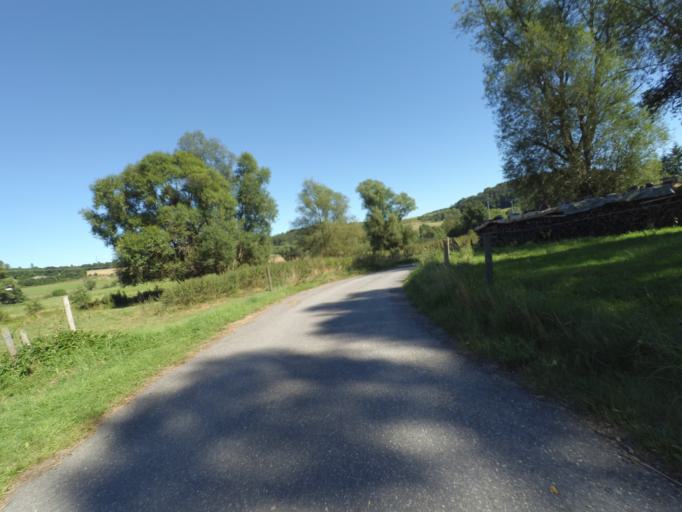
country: DE
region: Rheinland-Pfalz
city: Daun
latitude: 50.2085
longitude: 6.7946
